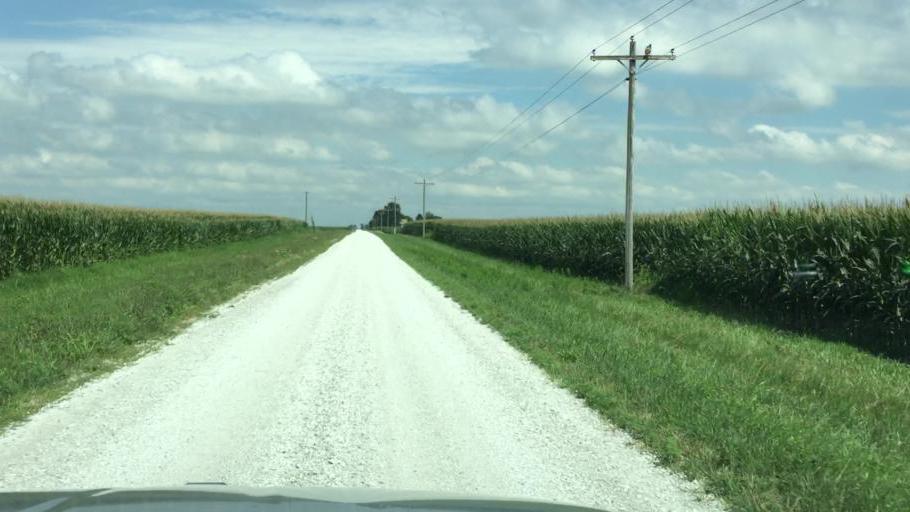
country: US
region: Illinois
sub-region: Hancock County
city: Nauvoo
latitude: 40.5218
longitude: -91.3004
